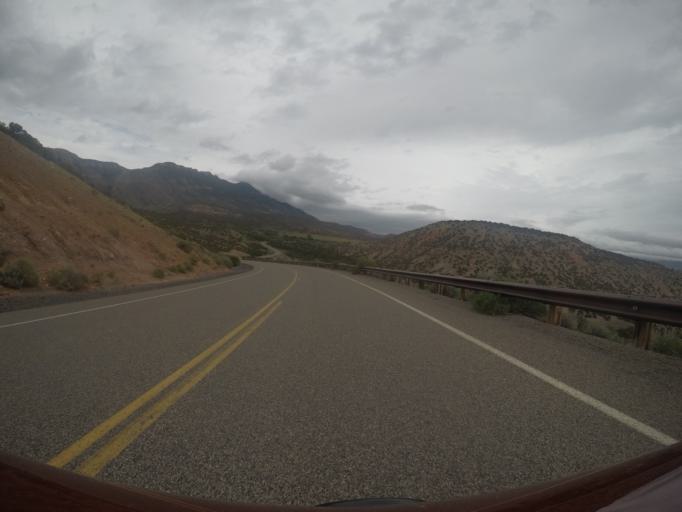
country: US
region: Wyoming
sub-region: Big Horn County
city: Lovell
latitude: 45.0762
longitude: -108.2581
